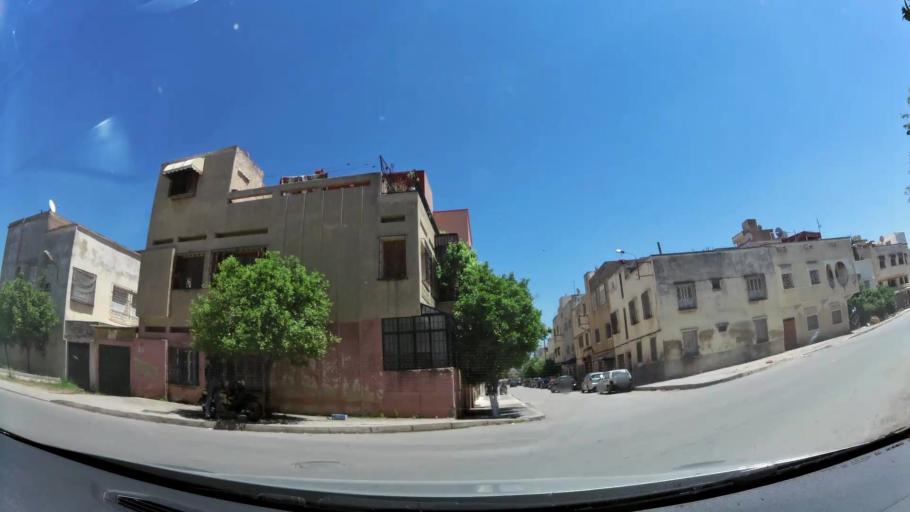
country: MA
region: Fes-Boulemane
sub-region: Fes
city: Fes
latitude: 34.0270
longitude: -5.0089
